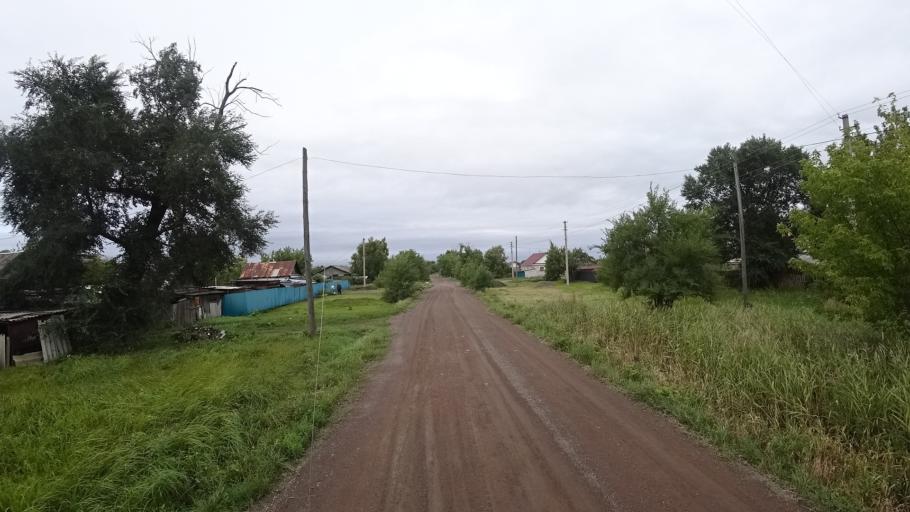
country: RU
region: Primorskiy
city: Chernigovka
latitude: 44.3335
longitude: 132.5692
